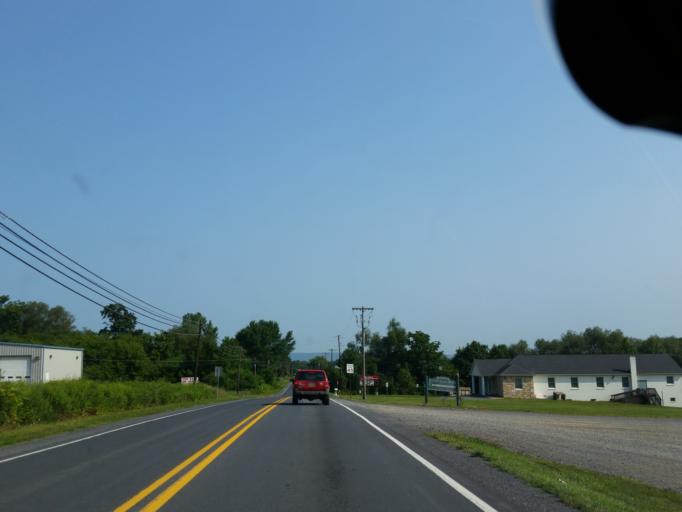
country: US
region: Pennsylvania
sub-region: Union County
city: New Columbia
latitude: 41.0319
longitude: -76.8661
